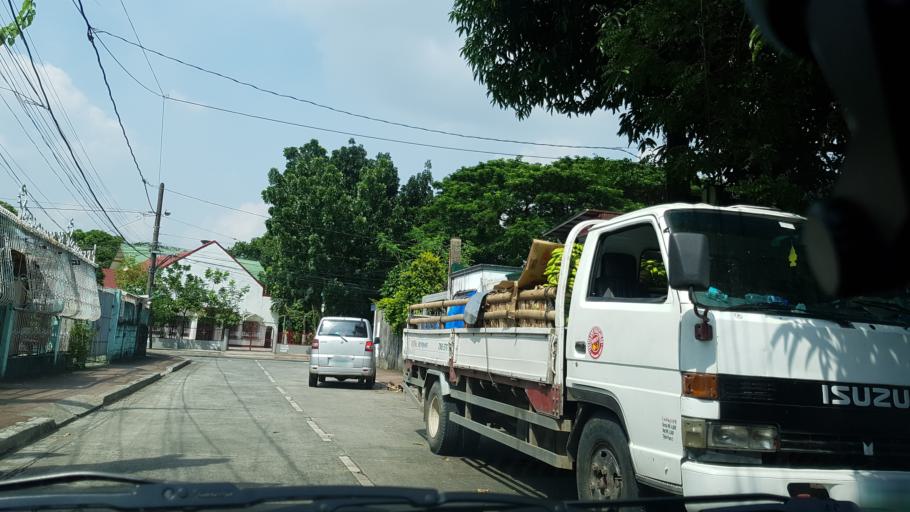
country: PH
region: Calabarzon
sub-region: Province of Rizal
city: San Mateo
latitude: 14.6652
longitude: 121.1124
